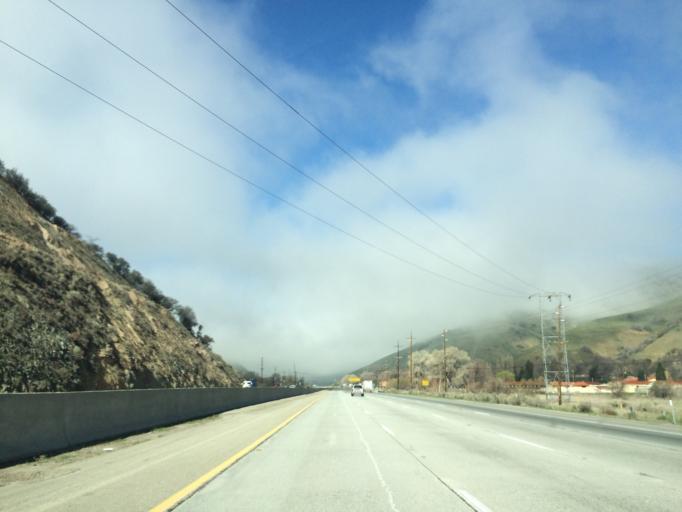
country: US
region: California
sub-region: Kern County
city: Lebec
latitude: 34.8688
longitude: -118.8861
